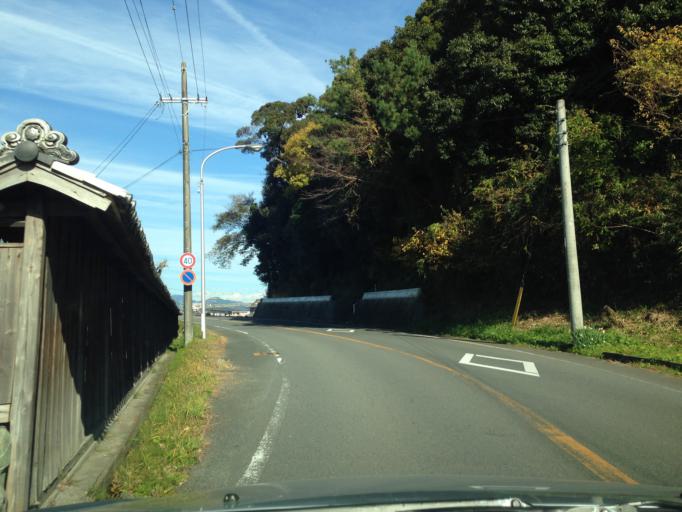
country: JP
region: Shizuoka
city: Kakegawa
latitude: 34.7672
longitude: 137.9832
